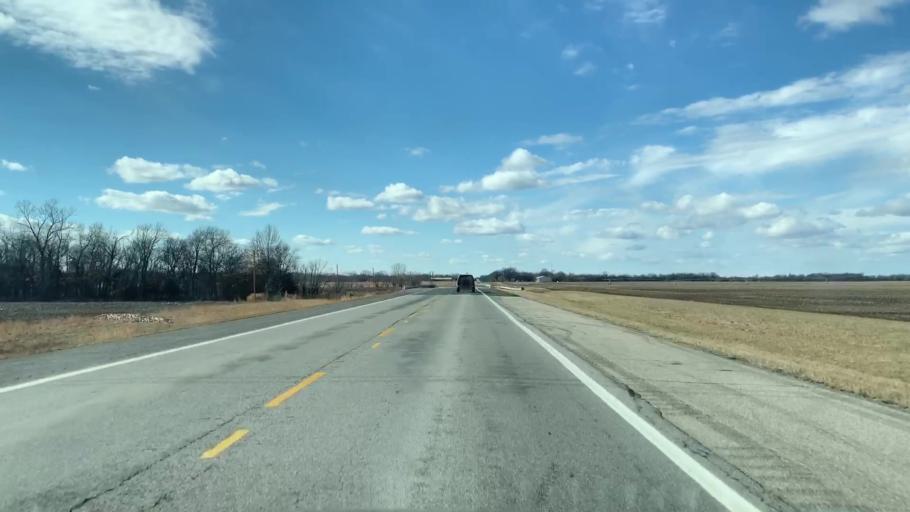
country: US
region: Kansas
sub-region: Labette County
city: Parsons
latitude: 37.3403
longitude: -95.1171
